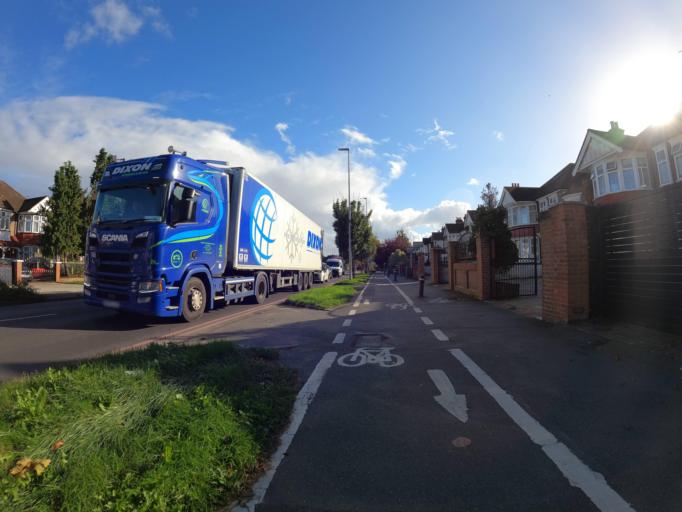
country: GB
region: England
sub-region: Greater London
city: Acton
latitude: 51.5040
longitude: -0.2893
